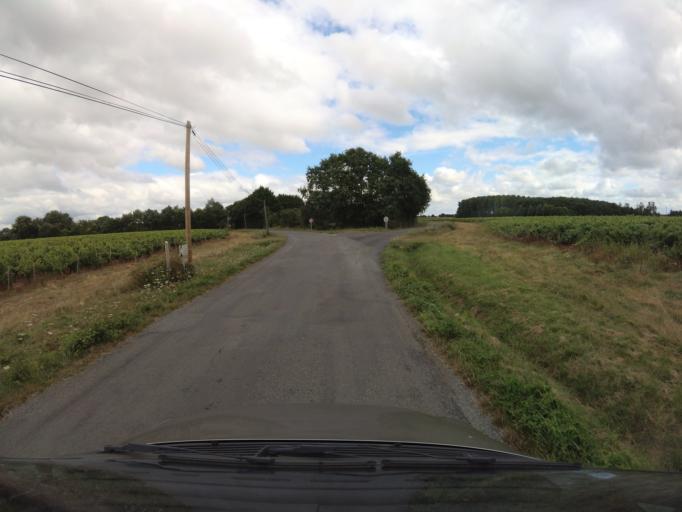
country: FR
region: Pays de la Loire
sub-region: Departement de la Vendee
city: Saint-Philbert-de-Bouaine
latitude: 47.0054
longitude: -1.5307
